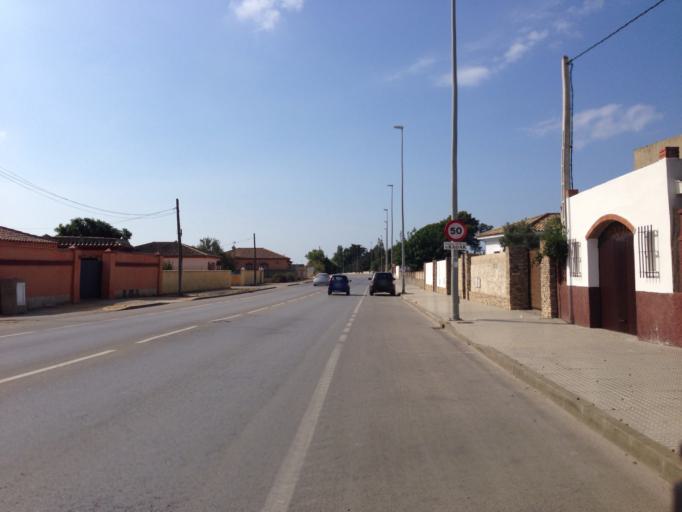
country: ES
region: Andalusia
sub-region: Provincia de Cadiz
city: Chiclana de la Frontera
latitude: 36.4061
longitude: -6.1663
